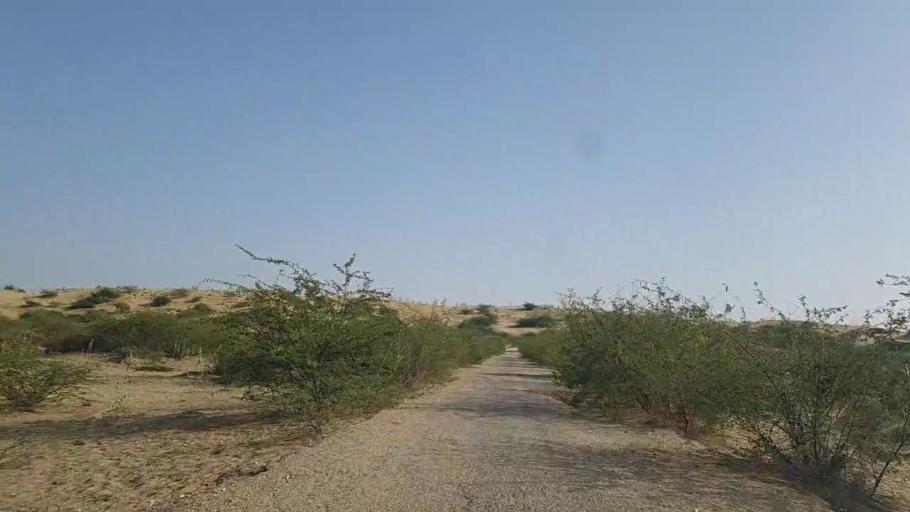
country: PK
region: Sindh
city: Naukot
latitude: 24.6198
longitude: 69.3716
